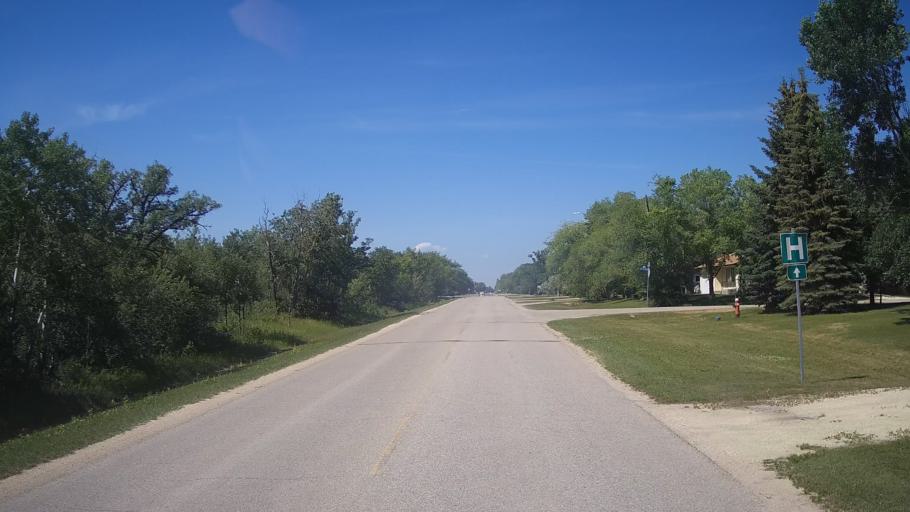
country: CA
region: Manitoba
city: Stonewall
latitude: 50.1245
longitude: -97.3333
